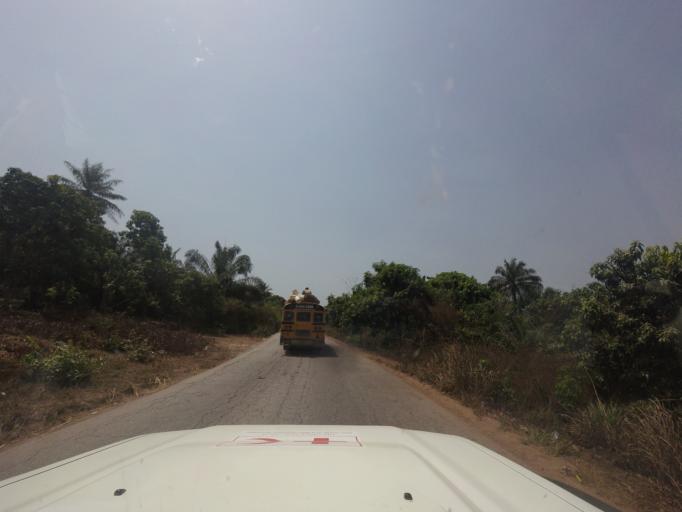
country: GN
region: Kindia
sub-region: Kindia
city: Kindia
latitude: 9.9167
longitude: -12.9970
